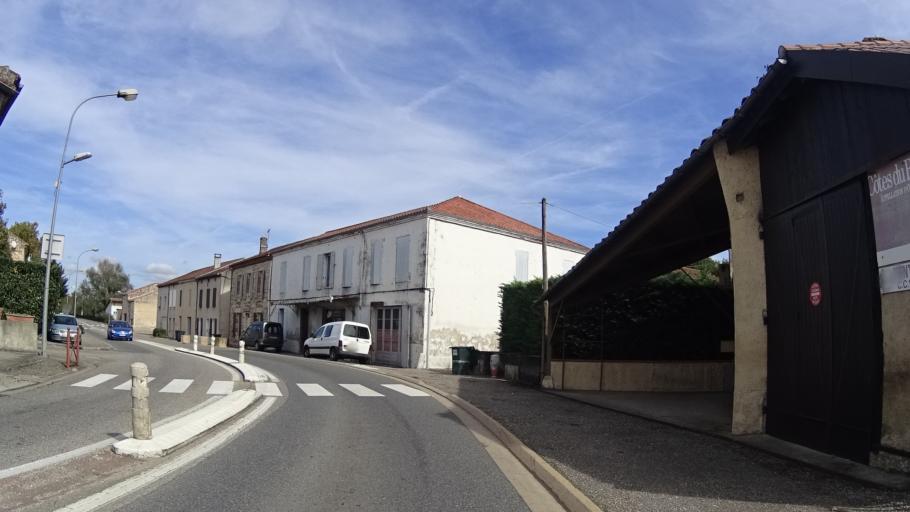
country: FR
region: Aquitaine
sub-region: Departement du Lot-et-Garonne
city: Layrac
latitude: 44.1344
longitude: 0.6641
